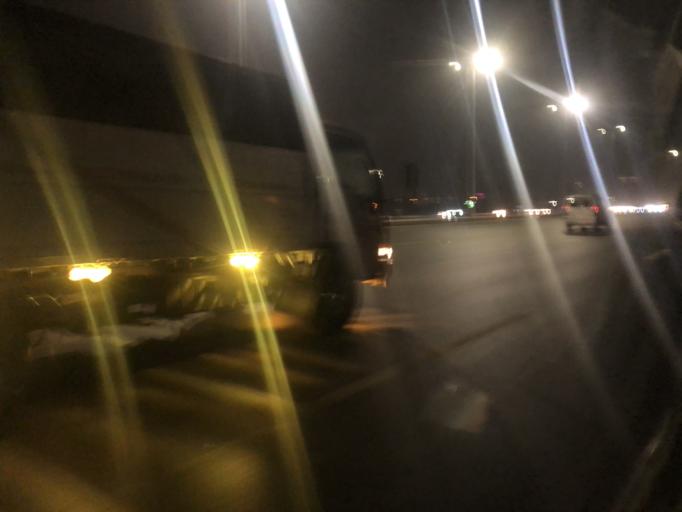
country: EG
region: Al Jizah
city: Al Jizah
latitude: 29.9856
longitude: 31.1256
